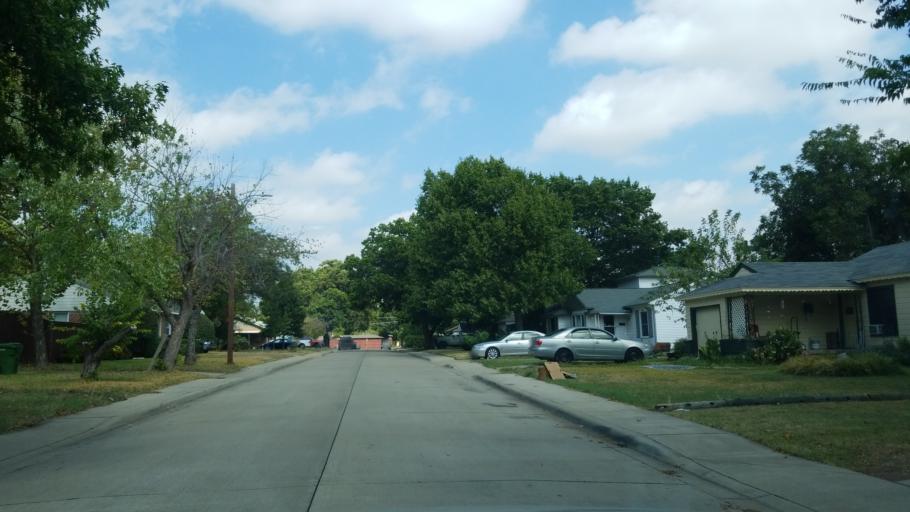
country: US
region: Texas
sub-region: Dallas County
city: Garland
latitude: 32.8928
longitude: -96.6524
